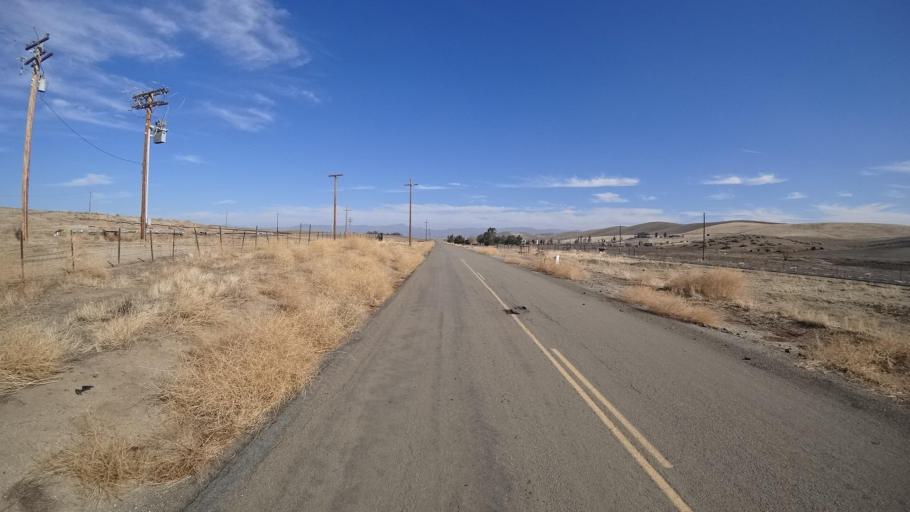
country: US
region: California
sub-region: Kern County
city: Oildale
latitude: 35.6262
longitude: -118.9827
